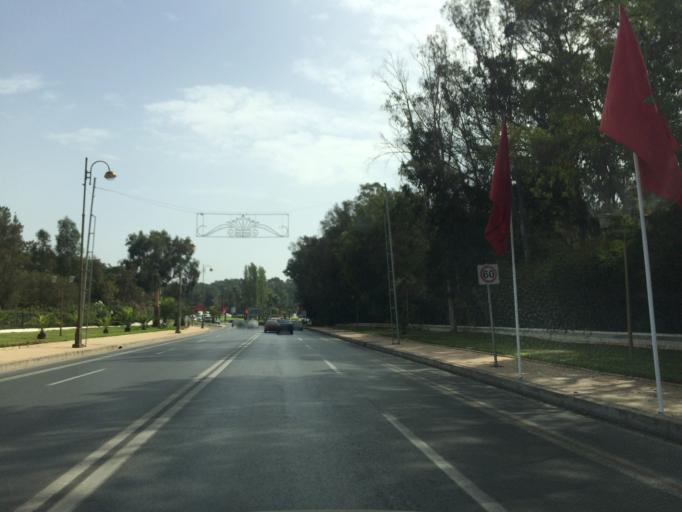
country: MA
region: Rabat-Sale-Zemmour-Zaer
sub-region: Rabat
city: Rabat
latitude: 33.9958
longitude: -6.8374
